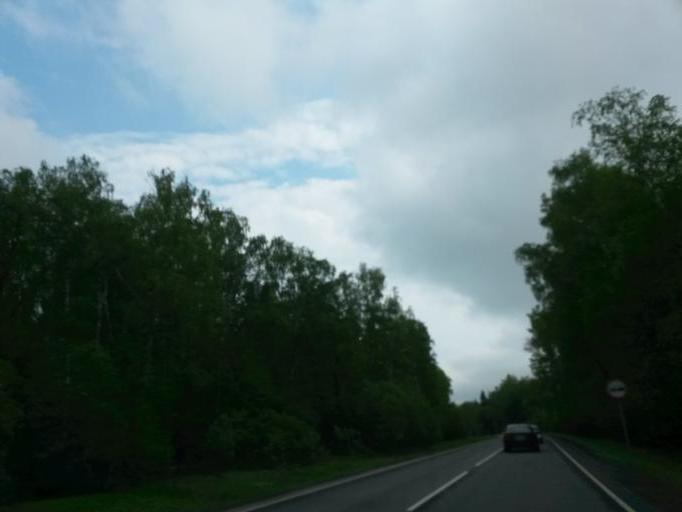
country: RU
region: Moskovskaya
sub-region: Podol'skiy Rayon
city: Podol'sk
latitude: 55.3787
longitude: 37.6364
